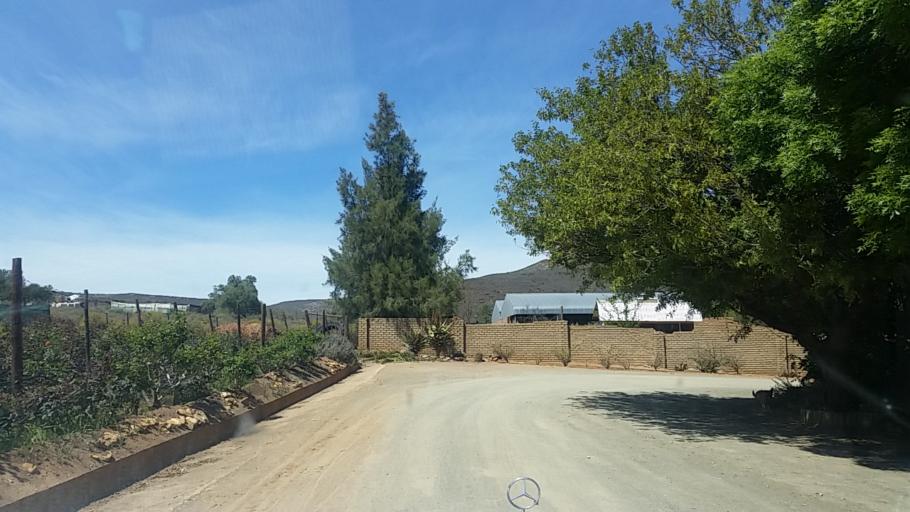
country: ZA
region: Western Cape
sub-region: Eden District Municipality
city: Knysna
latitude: -33.6502
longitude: 23.1356
